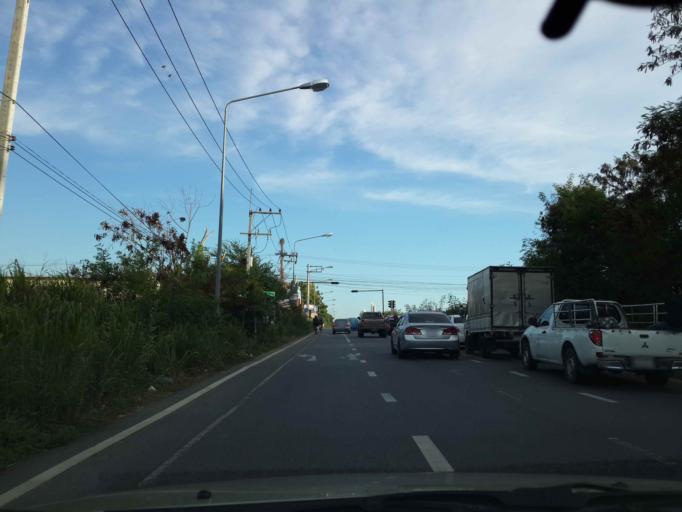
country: TH
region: Chon Buri
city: Phatthaya
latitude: 12.9006
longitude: 100.9007
